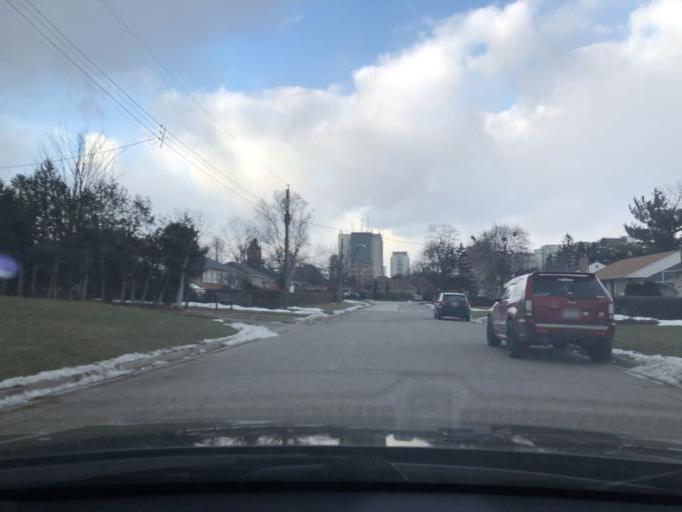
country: CA
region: Ontario
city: Scarborough
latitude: 43.7791
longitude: -79.2901
